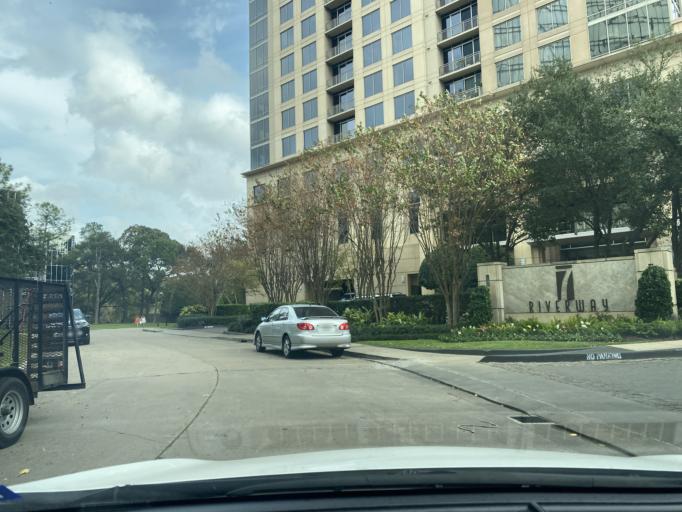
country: US
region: Texas
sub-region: Harris County
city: Hunters Creek Village
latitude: 29.7616
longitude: -95.4620
